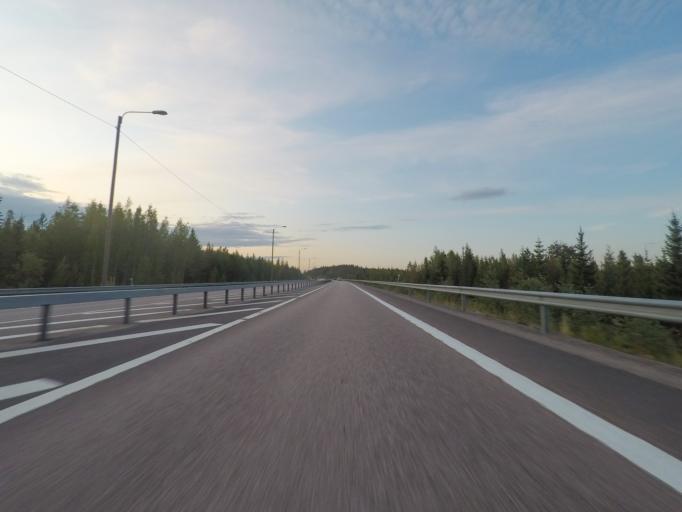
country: FI
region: Central Finland
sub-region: Jyvaeskylae
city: Saeynaetsalo
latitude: 62.1724
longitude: 25.9061
